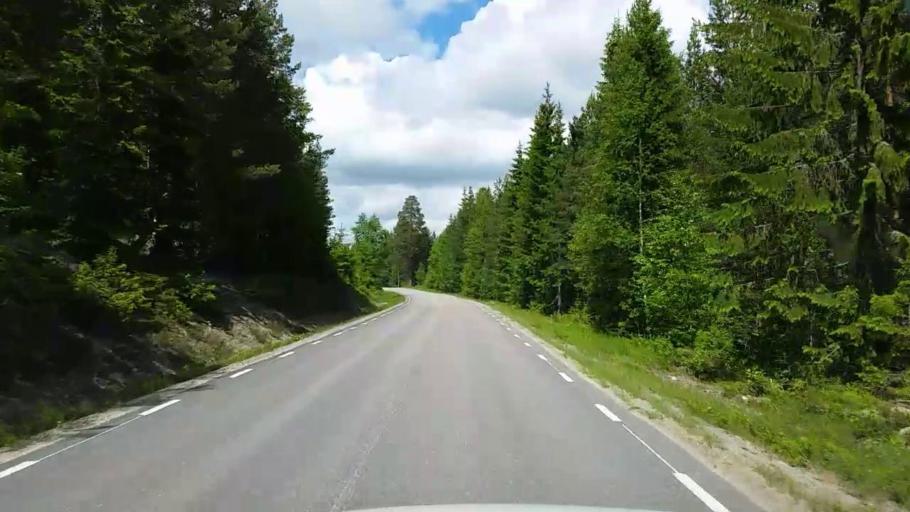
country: SE
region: Gaevleborg
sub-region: Bollnas Kommun
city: Vittsjo
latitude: 61.1036
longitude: 16.1600
